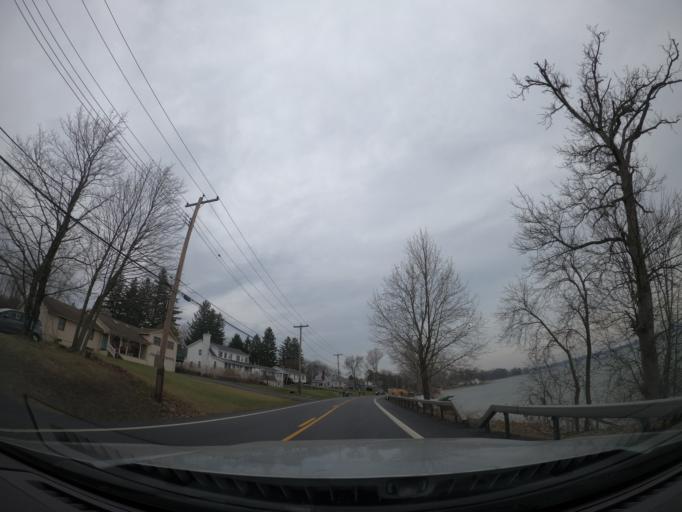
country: US
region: New York
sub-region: Cayuga County
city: Melrose Park
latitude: 42.8766
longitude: -76.5427
